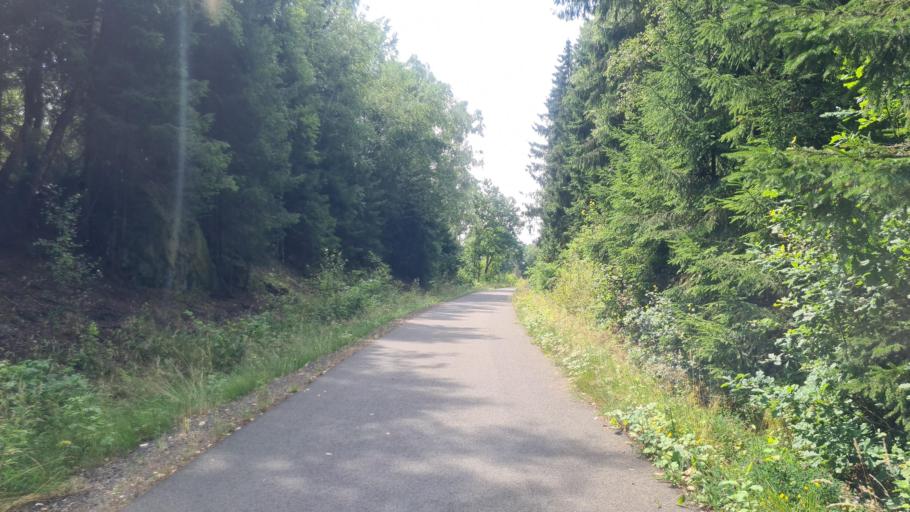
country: SE
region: Kronoberg
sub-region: Ljungby Kommun
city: Ljungby
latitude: 56.8598
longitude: 13.9772
